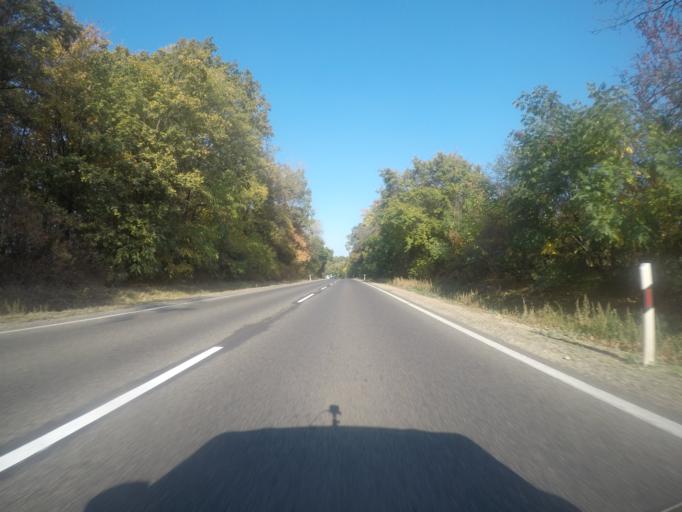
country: HU
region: Fejer
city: dunaujvaros
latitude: 46.9935
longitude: 18.9258
